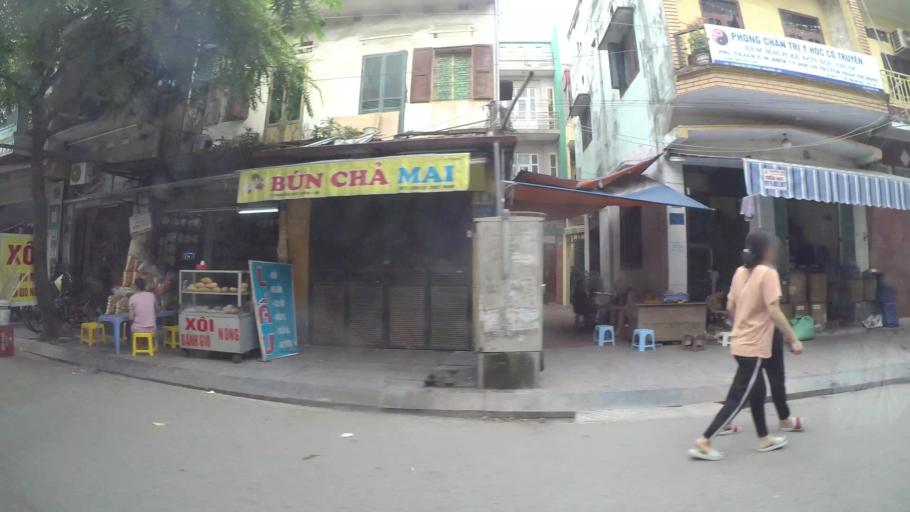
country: VN
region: Ha Noi
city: Ha Dong
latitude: 20.9701
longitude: 105.7740
